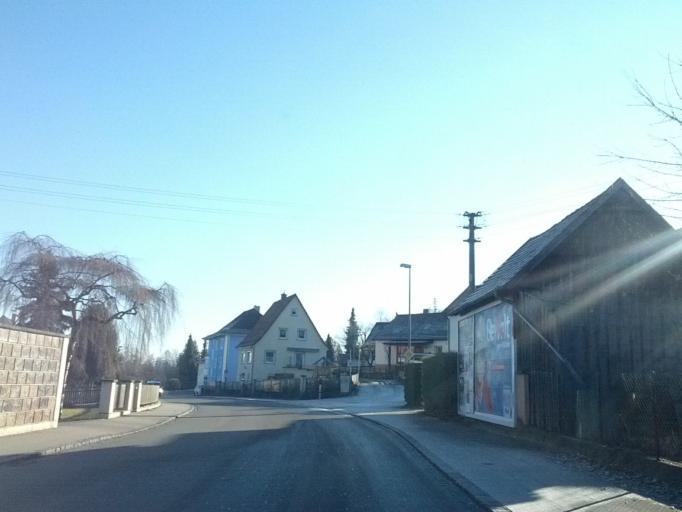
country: DE
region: Bavaria
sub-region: Swabia
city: Buxheim
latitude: 47.9943
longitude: 10.1373
